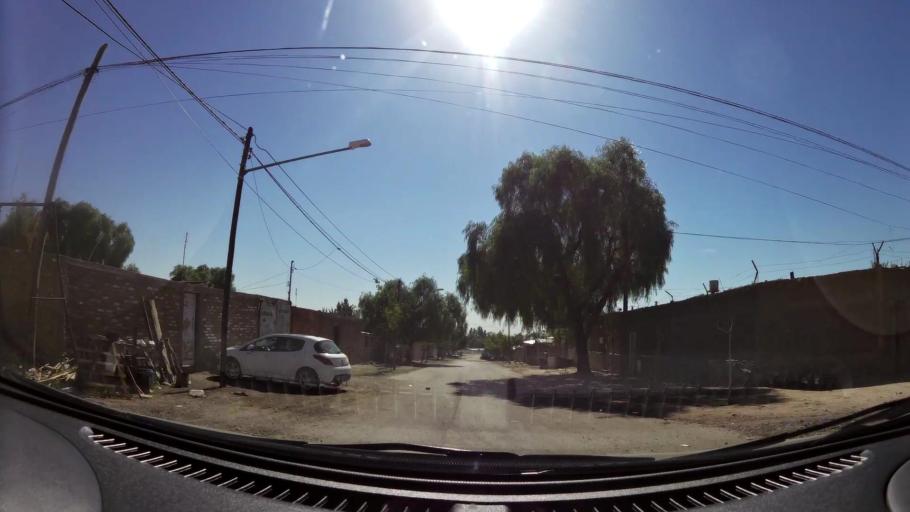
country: AR
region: Mendoza
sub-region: Departamento de Godoy Cruz
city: Godoy Cruz
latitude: -32.9119
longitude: -68.8836
